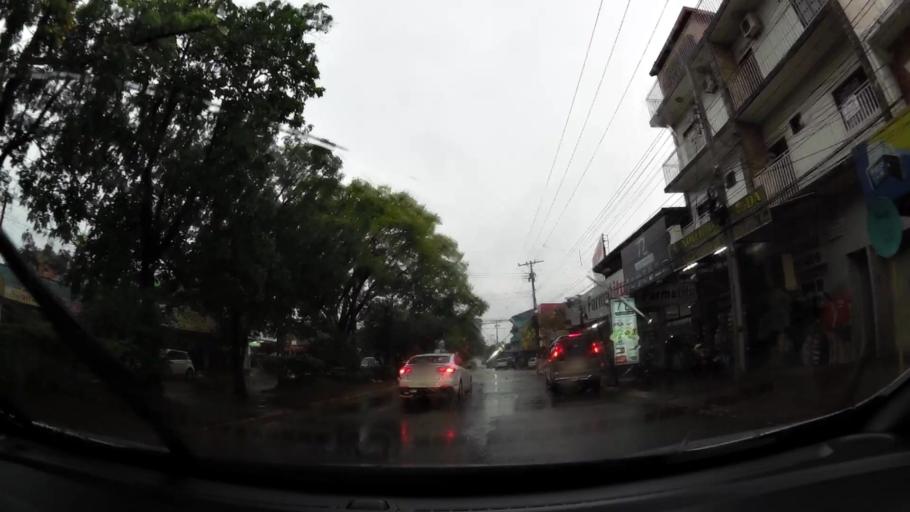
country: PY
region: Alto Parana
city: Ciudad del Este
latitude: -25.5063
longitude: -54.6697
